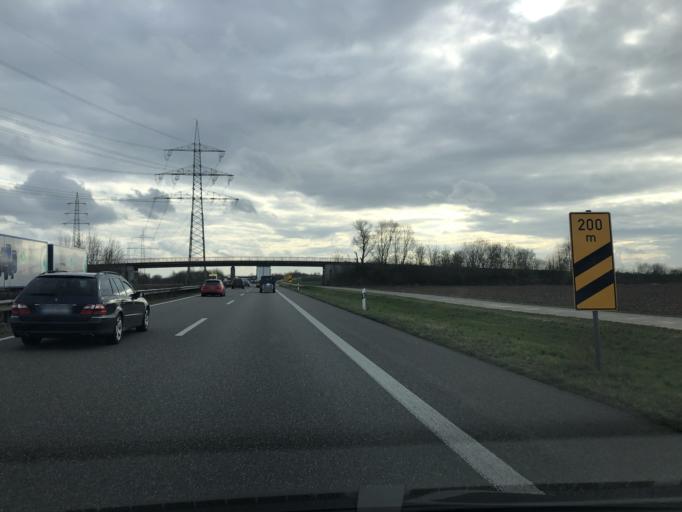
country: DE
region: Rheinland-Pfalz
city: Rulzheim
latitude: 49.1753
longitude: 8.3039
